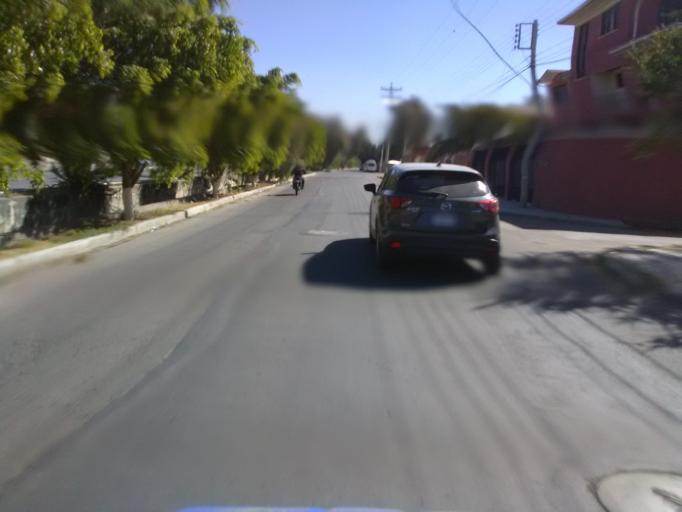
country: BO
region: Cochabamba
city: Cochabamba
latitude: -17.3816
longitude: -66.1953
